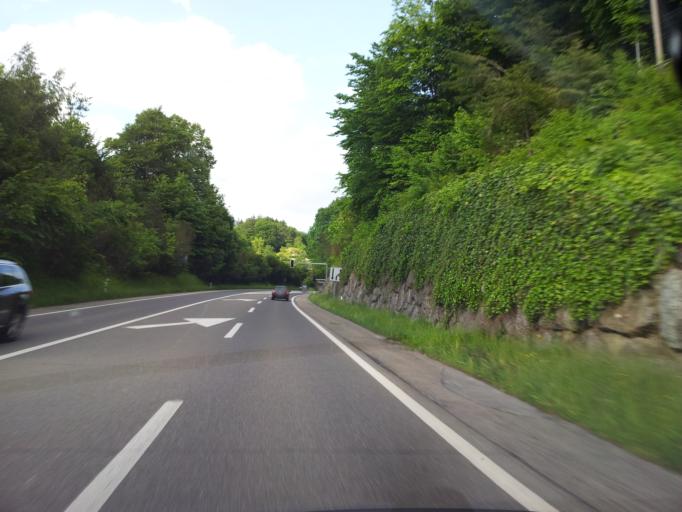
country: CH
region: Bern
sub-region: Interlaken-Oberhasli District
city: Ringgenberg
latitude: 46.7014
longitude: 7.9455
